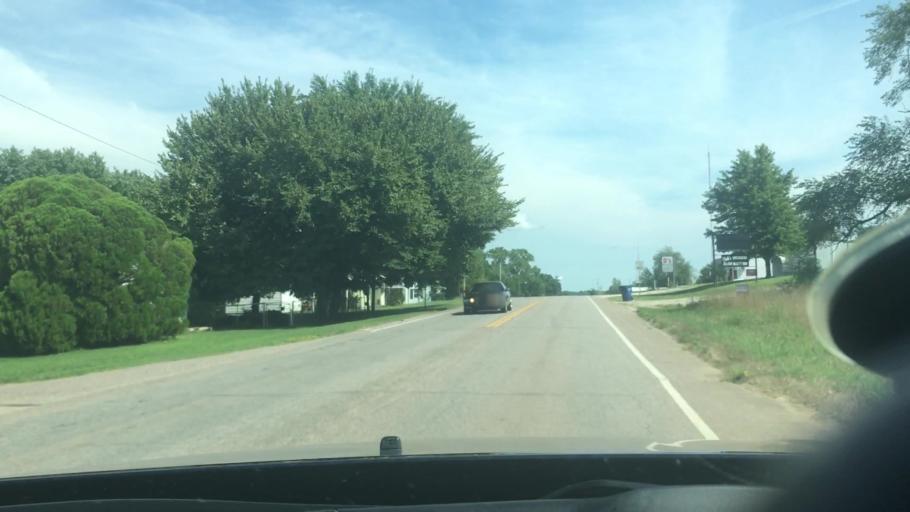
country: US
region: Oklahoma
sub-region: Seminole County
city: Seminole
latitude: 35.2309
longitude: -96.6856
